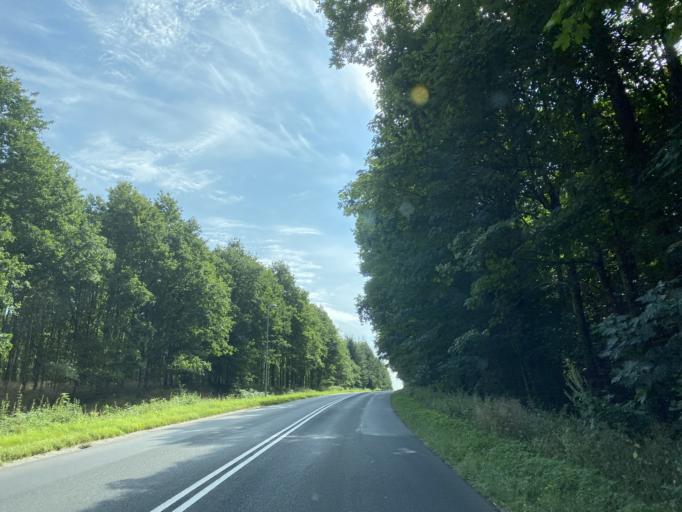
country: DK
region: Central Jutland
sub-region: Favrskov Kommune
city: Hammel
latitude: 56.2638
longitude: 9.8430
